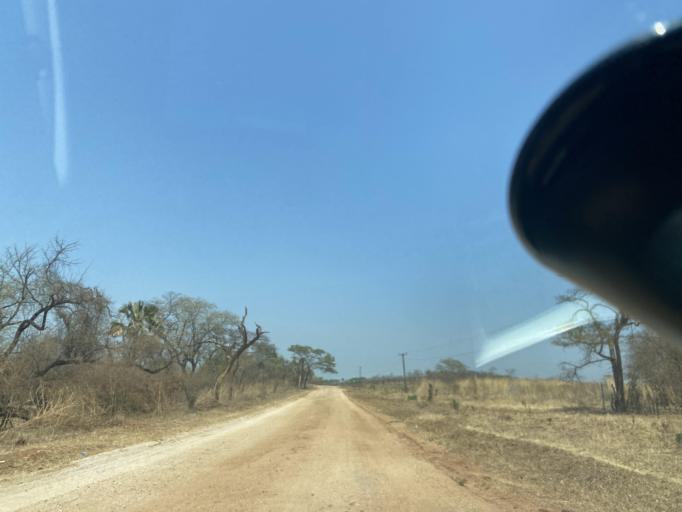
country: ZM
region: Lusaka
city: Lusaka
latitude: -15.5406
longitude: 28.0771
